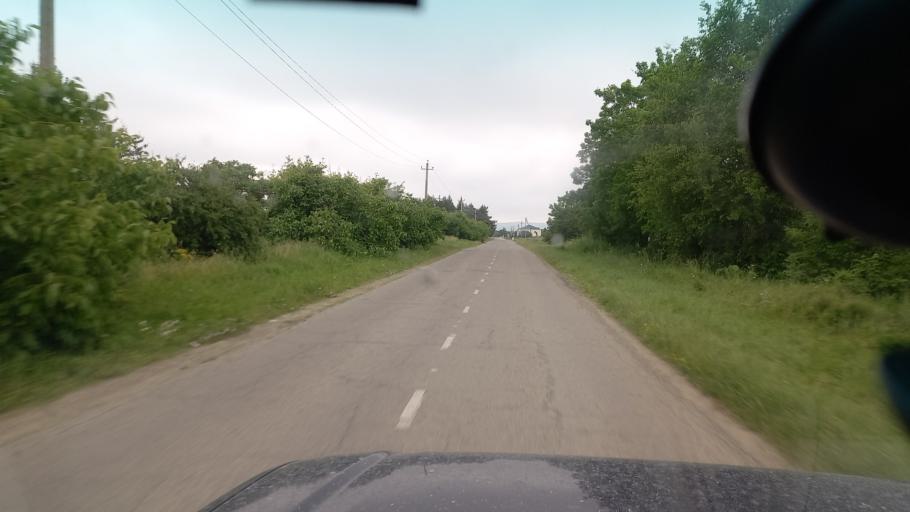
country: RU
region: Krasnodarskiy
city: Mostovskoy
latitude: 44.4231
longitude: 40.7682
